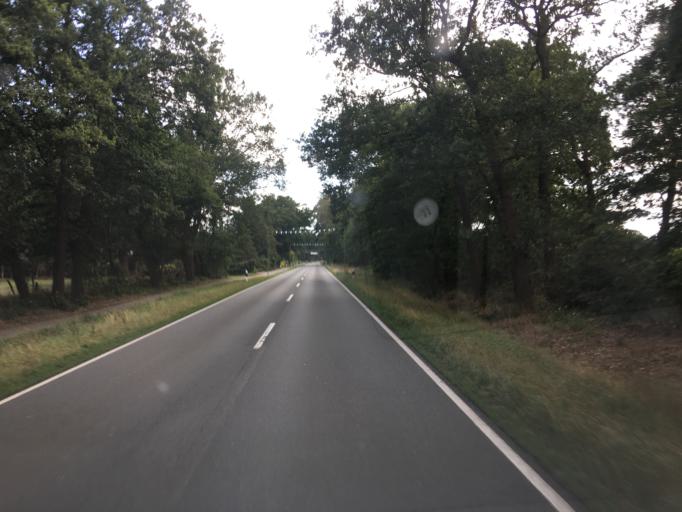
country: DE
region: Lower Saxony
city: Friesoythe
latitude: 53.0720
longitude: 7.8460
